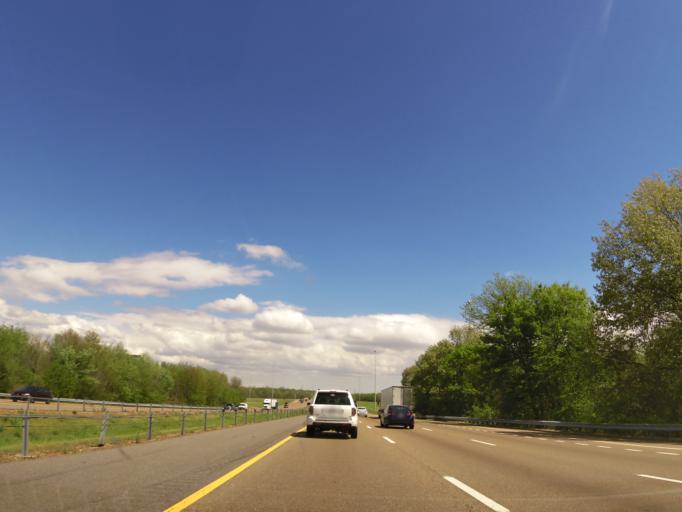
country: US
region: Tennessee
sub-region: Shelby County
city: Bartlett
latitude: 35.1908
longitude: -89.9632
